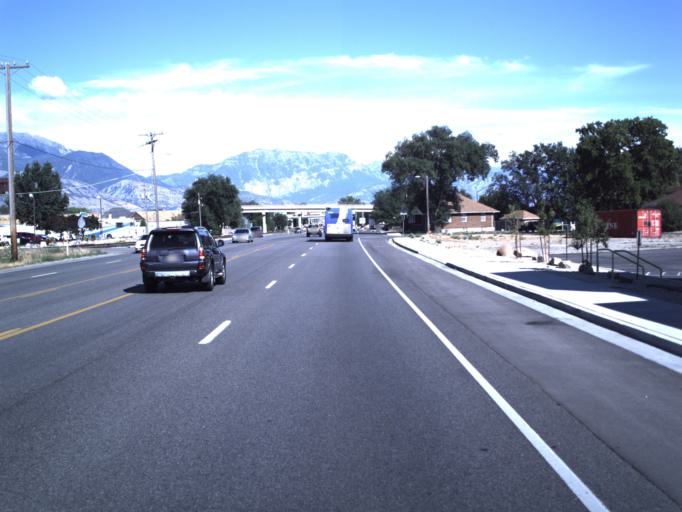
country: US
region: Utah
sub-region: Utah County
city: Lehi
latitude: 40.3957
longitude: -111.8444
